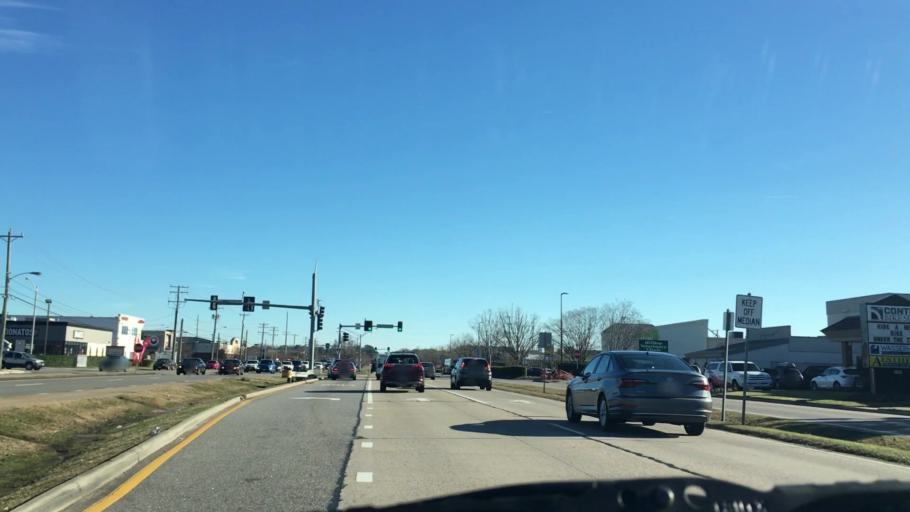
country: US
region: Virginia
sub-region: City of Virginia Beach
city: Virginia Beach
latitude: 36.8496
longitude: -76.0281
